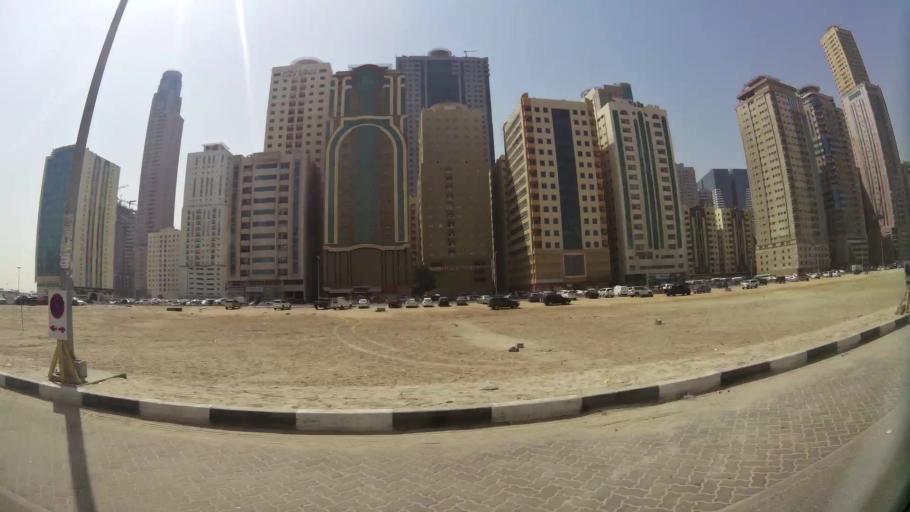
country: AE
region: Ash Shariqah
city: Sharjah
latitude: 25.3059
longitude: 55.3786
